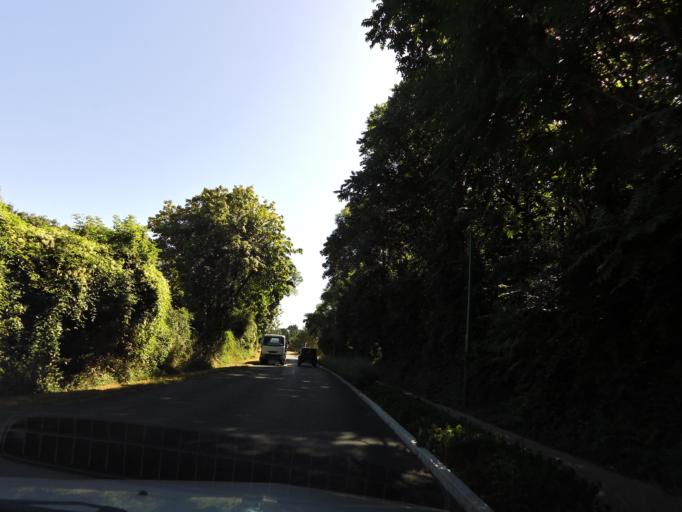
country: FR
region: Pays de la Loire
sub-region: Departement de la Vendee
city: Jard-sur-Mer
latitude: 46.4152
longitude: -1.5432
